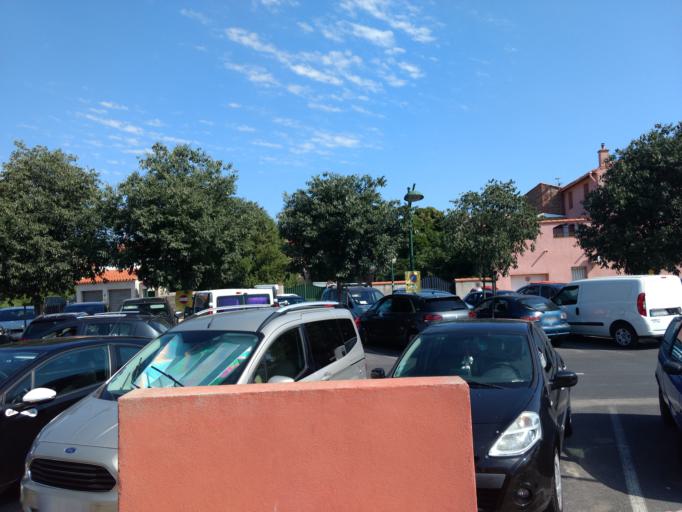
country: FR
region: Languedoc-Roussillon
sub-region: Departement des Pyrenees-Orientales
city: Bompas
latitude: 42.7307
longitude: 2.9328
